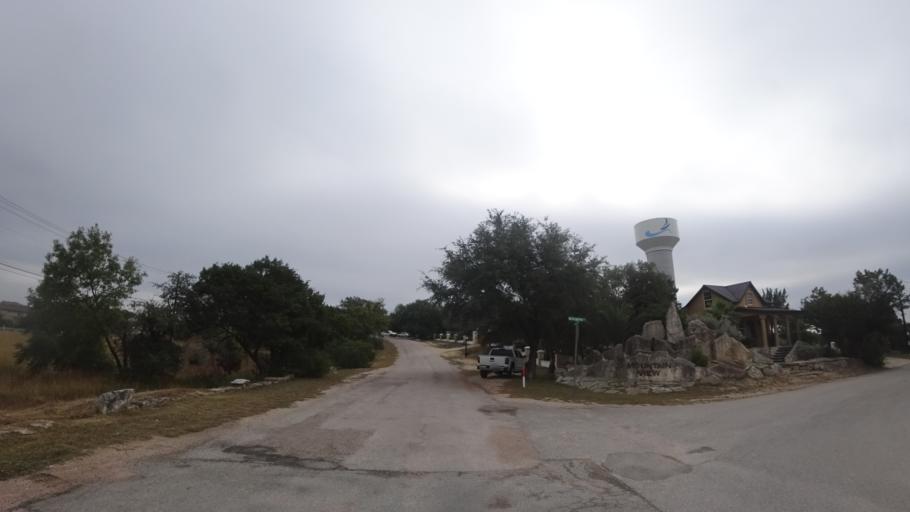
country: US
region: Texas
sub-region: Travis County
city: Hudson Bend
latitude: 30.3963
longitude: -97.9224
